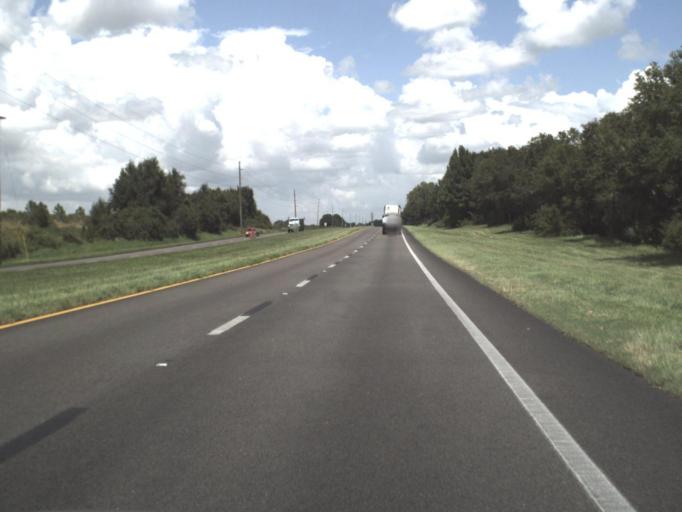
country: US
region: Florida
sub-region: Polk County
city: Fort Meade
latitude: 27.7949
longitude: -81.8155
